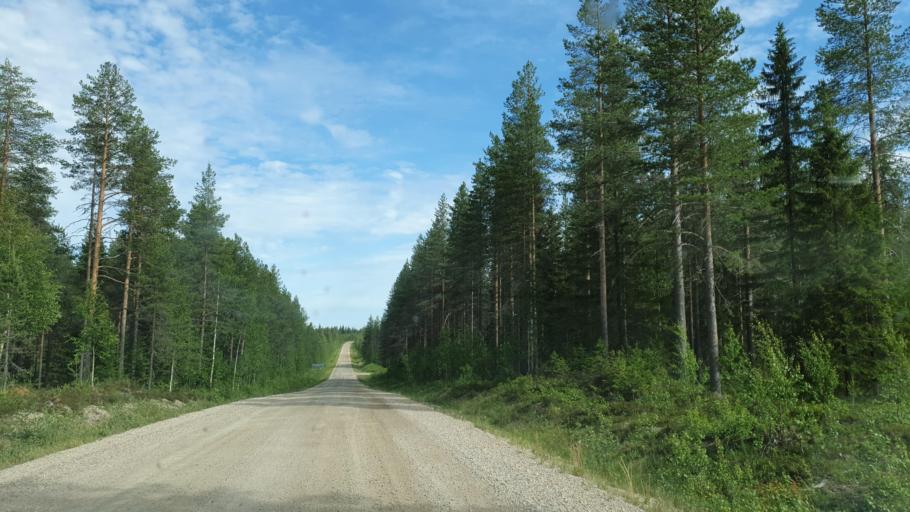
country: FI
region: Kainuu
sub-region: Kehys-Kainuu
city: Kuhmo
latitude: 64.4904
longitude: 29.4998
